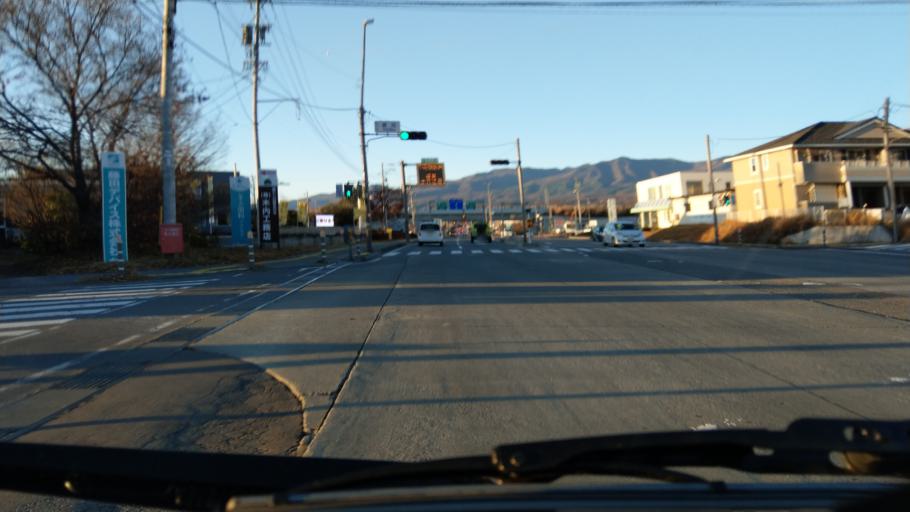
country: JP
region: Nagano
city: Komoro
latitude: 36.2917
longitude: 138.4707
